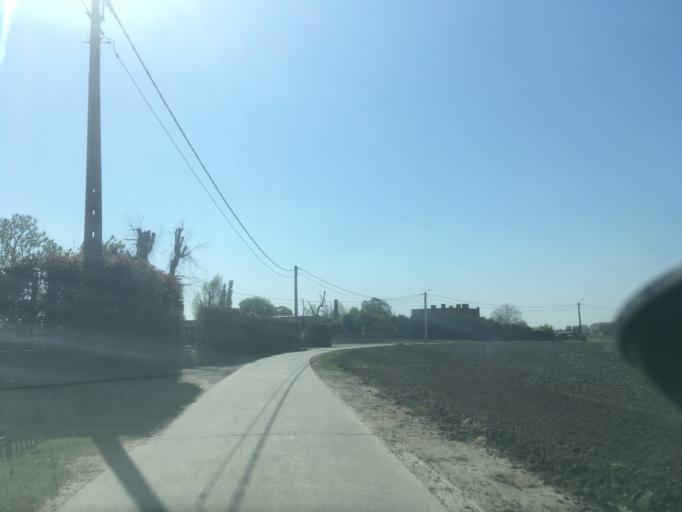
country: BE
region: Flanders
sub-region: Provincie West-Vlaanderen
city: Ardooie
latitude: 50.9613
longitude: 3.2184
